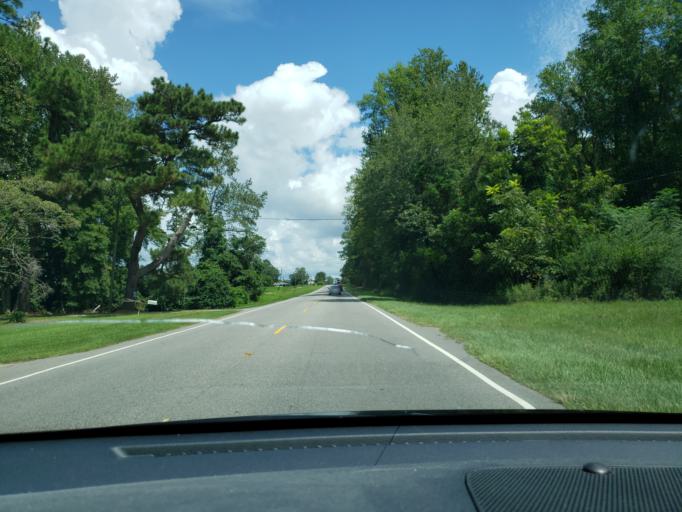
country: US
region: North Carolina
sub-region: Columbus County
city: Brunswick
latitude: 34.2524
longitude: -78.7515
